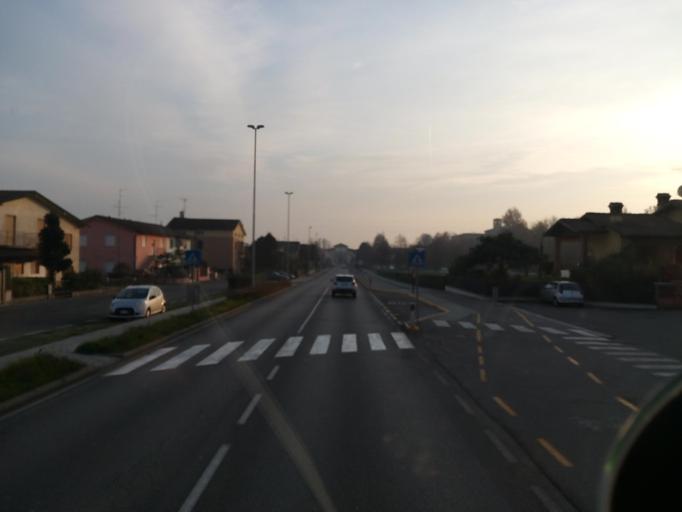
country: IT
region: Lombardy
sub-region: Provincia di Brescia
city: Poncarale
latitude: 45.4643
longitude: 10.1742
